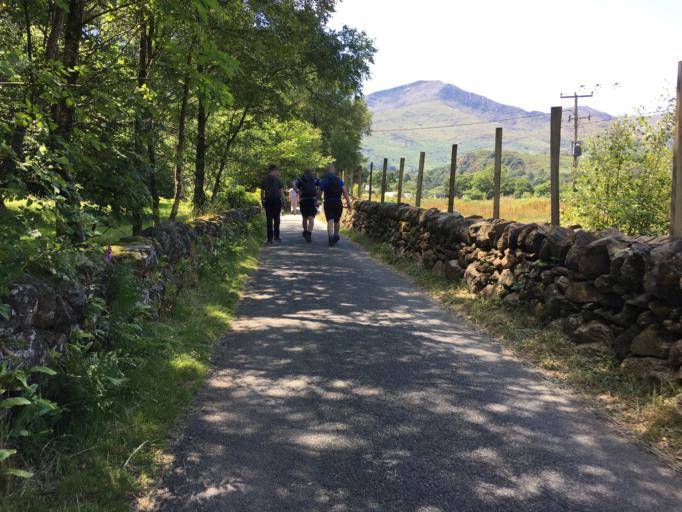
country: GB
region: Wales
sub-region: Gwynedd
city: Penrhyndeudraeth
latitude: 53.0182
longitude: -4.0849
